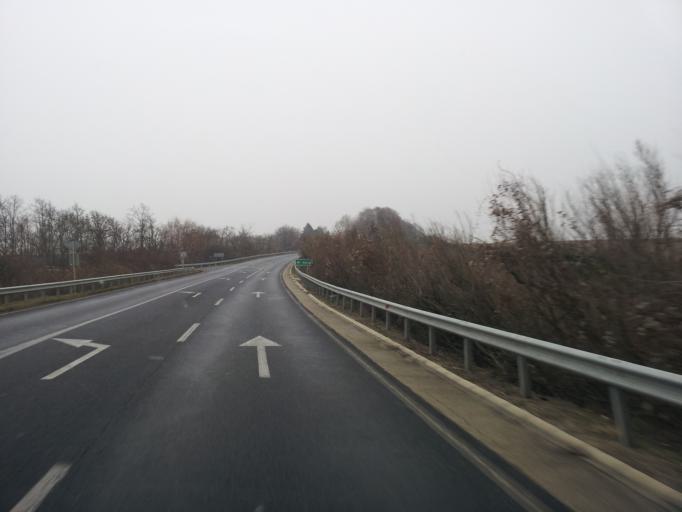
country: HU
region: Veszprem
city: Urkut
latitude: 47.1443
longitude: 17.6123
